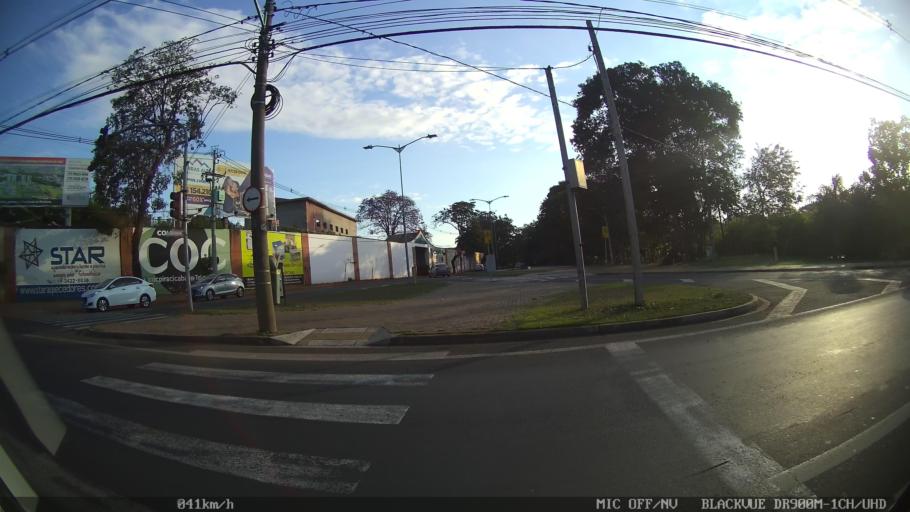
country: BR
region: Sao Paulo
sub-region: Piracicaba
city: Piracicaba
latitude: -22.7062
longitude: -47.6472
